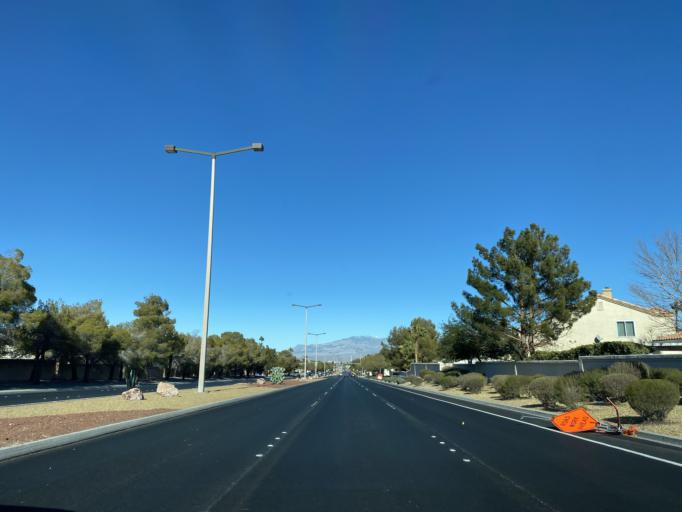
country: US
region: Nevada
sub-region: Clark County
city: Summerlin South
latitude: 36.2075
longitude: -115.2789
